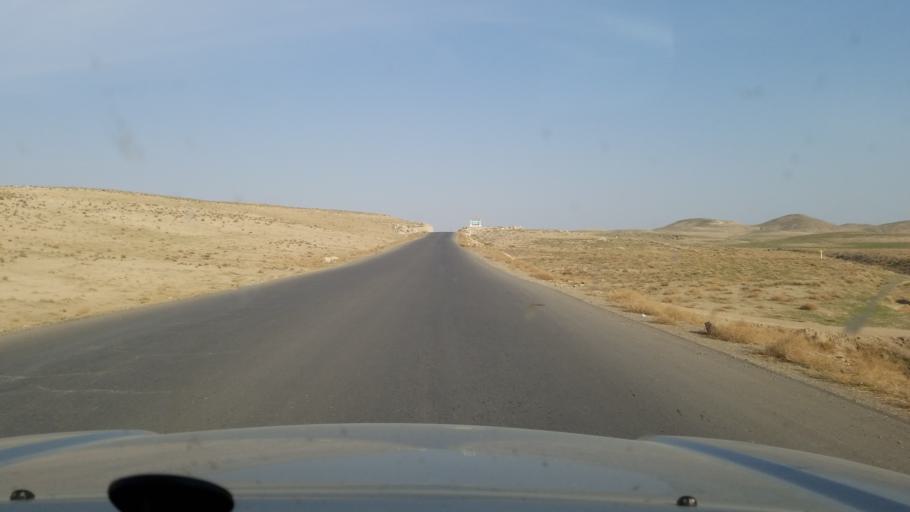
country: AF
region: Jowzjan
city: Khamyab
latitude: 37.6207
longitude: 65.7045
